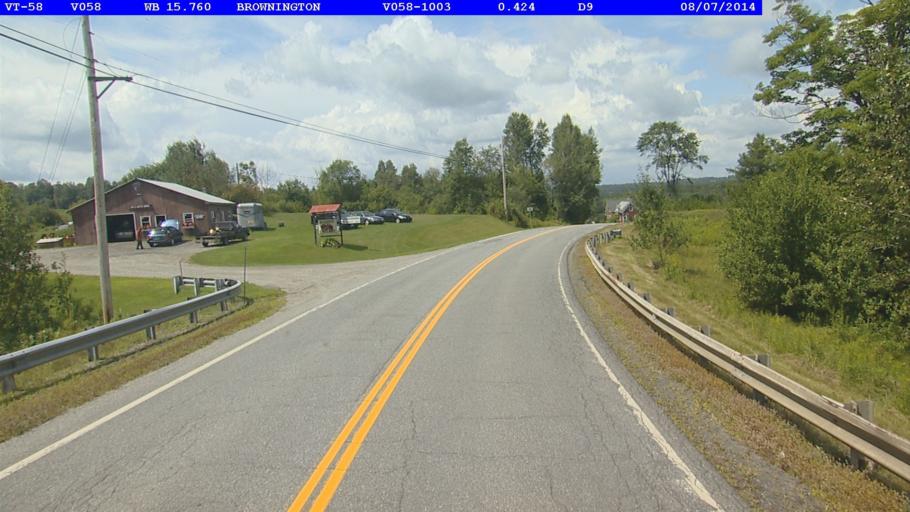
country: US
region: Vermont
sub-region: Orleans County
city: Newport
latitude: 44.8040
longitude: -72.1369
